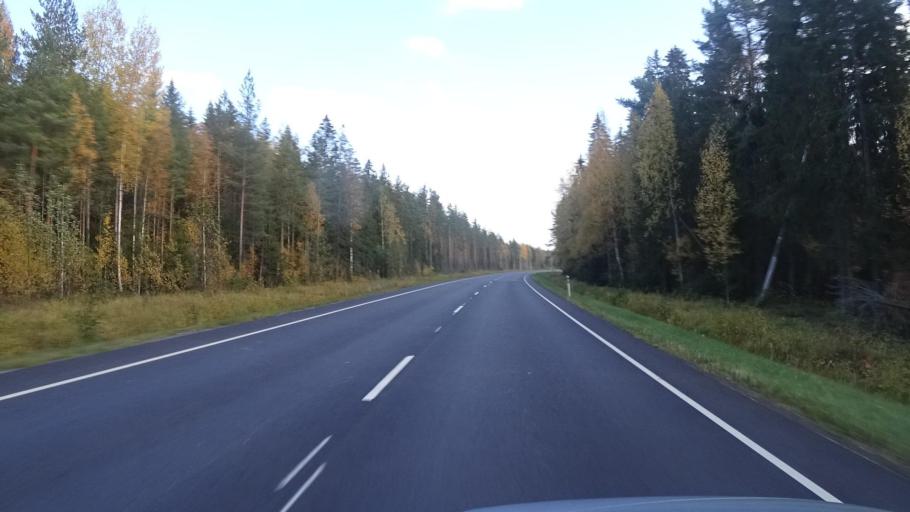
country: FI
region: Satakunta
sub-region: Rauma
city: Koeylioe
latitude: 61.1040
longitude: 22.2295
